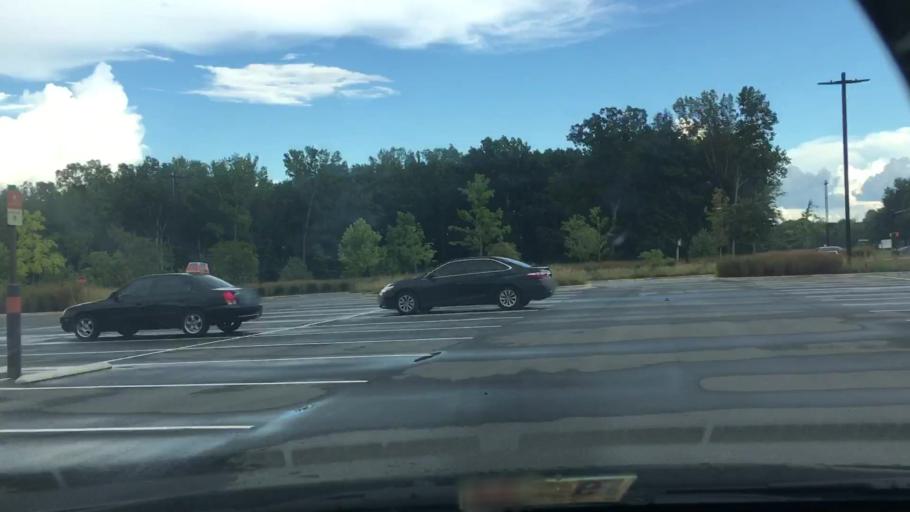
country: US
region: South Carolina
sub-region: York County
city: Fort Mill
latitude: 35.0249
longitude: -80.9618
